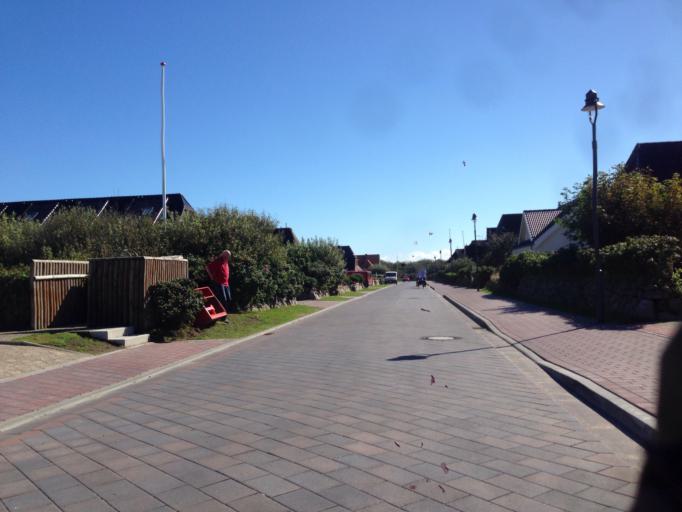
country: DE
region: Schleswig-Holstein
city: Westerland
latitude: 54.9395
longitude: 8.3223
